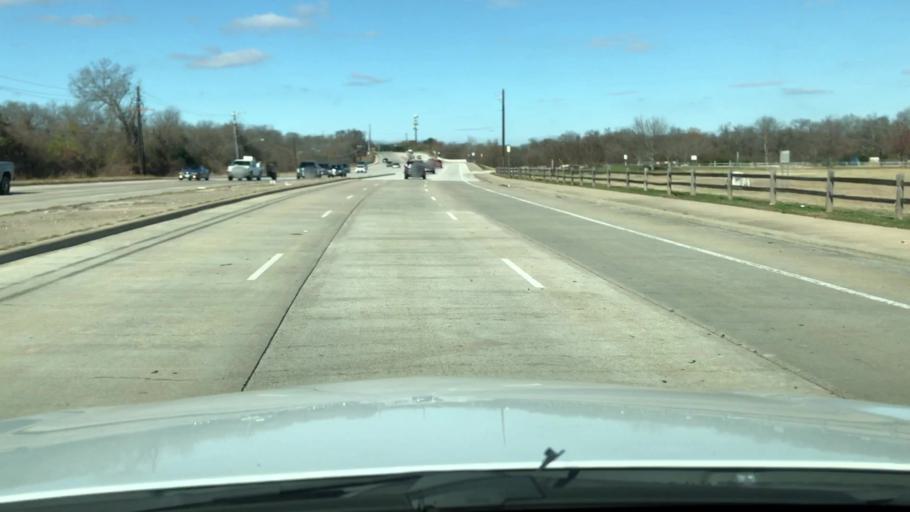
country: US
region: Texas
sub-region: Travis County
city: Onion Creek
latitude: 30.1752
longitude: -97.7430
